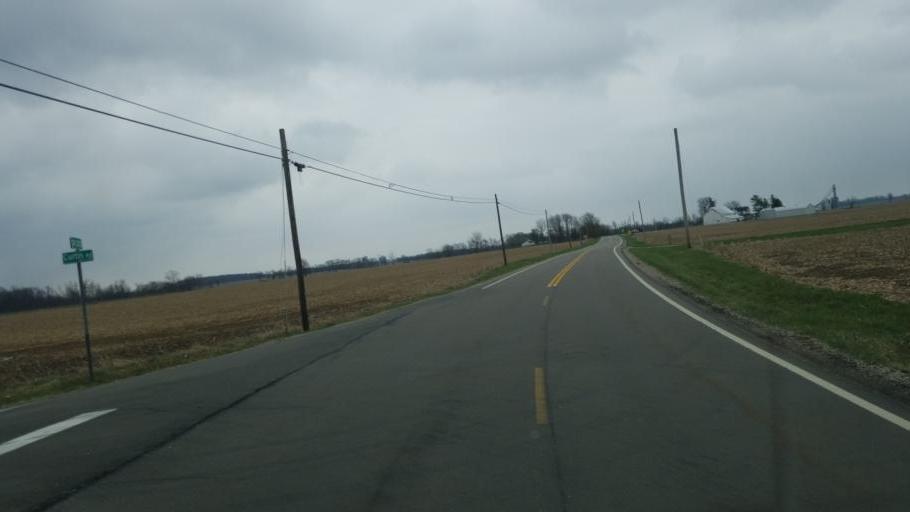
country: US
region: Ohio
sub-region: Marion County
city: Prospect
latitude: 40.4046
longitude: -83.1656
